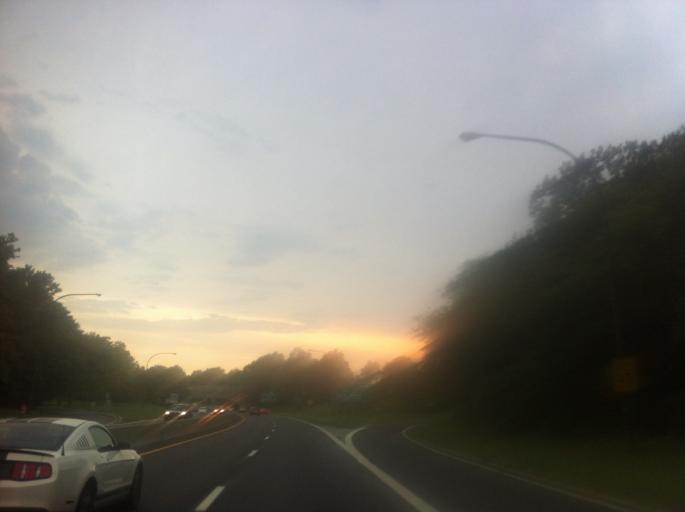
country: US
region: New York
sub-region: Nassau County
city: Plainview
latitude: 40.7952
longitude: -73.4897
